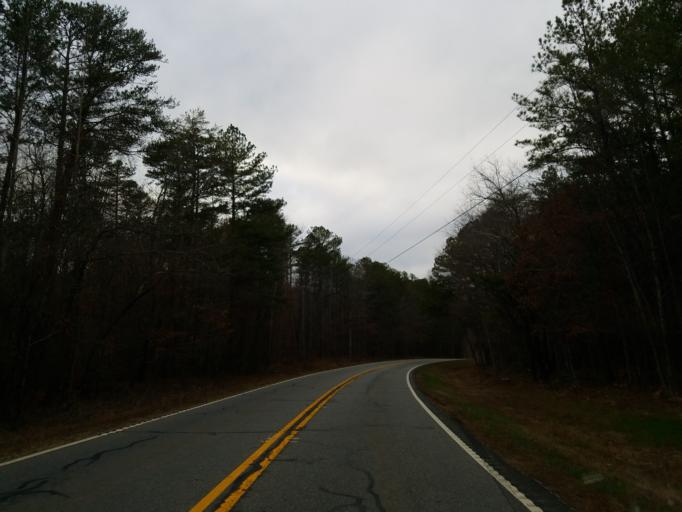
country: US
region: Georgia
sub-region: Bartow County
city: Rydal
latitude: 34.3418
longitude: -84.6335
